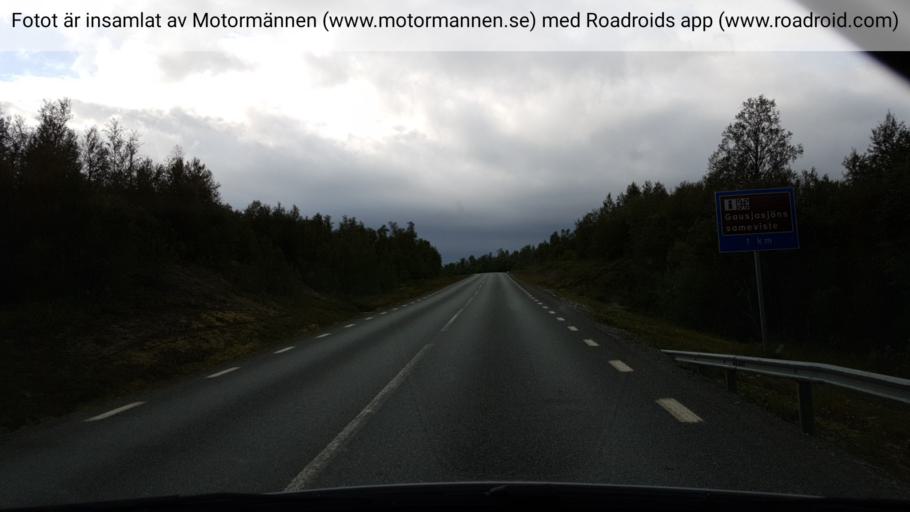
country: NO
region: Nordland
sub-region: Rana
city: Mo i Rana
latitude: 66.0658
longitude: 14.8736
